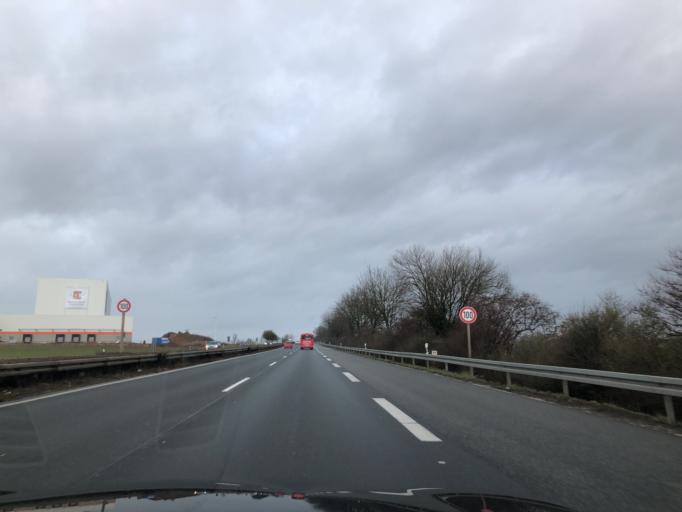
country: DE
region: Hesse
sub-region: Regierungsbezirk Giessen
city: Dehrn
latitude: 50.4100
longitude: 8.0772
